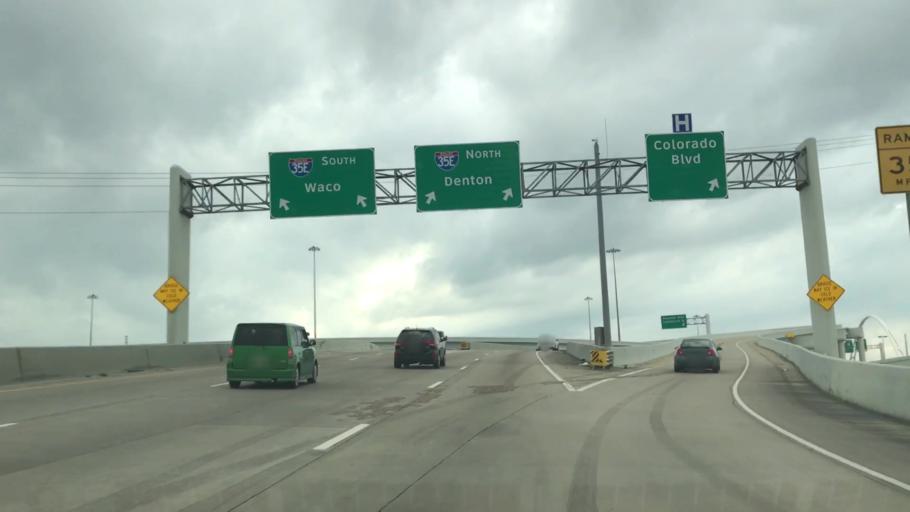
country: US
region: Texas
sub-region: Dallas County
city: Dallas
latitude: 32.7698
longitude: -96.8027
